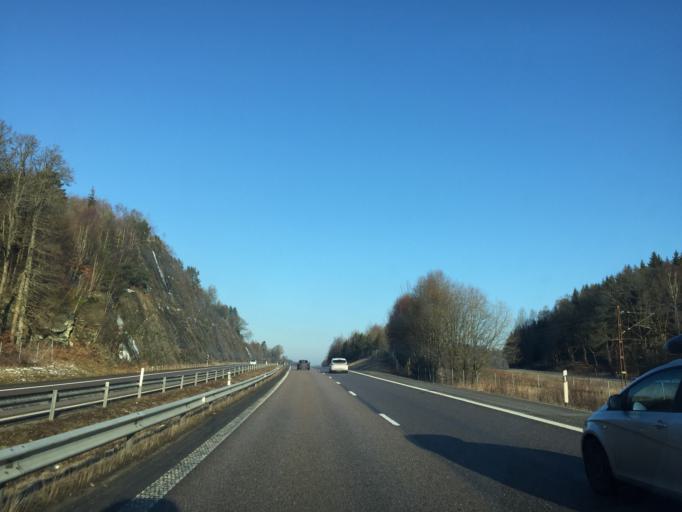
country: SE
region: Vaestra Goetaland
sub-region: Uddevalla Kommun
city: Ljungskile
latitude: 58.2534
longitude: 11.9031
